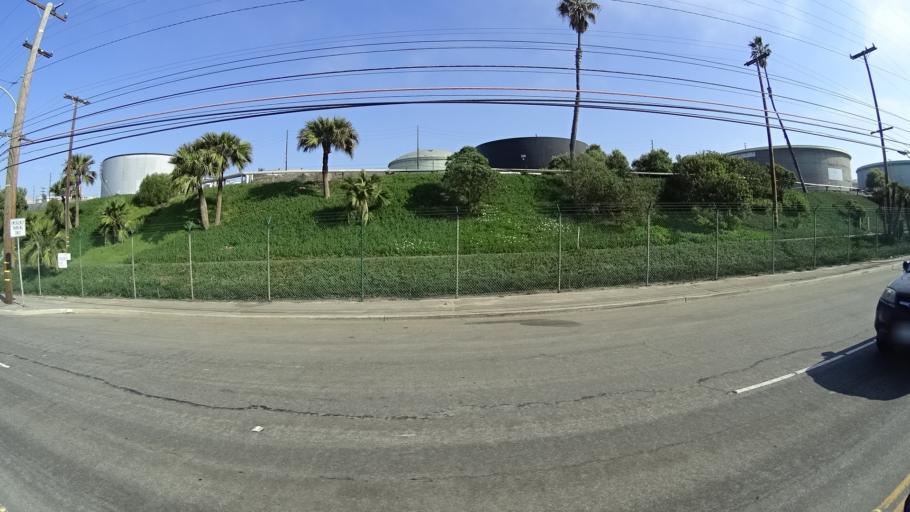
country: US
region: California
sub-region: Los Angeles County
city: El Segundo
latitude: 33.9106
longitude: -118.4235
